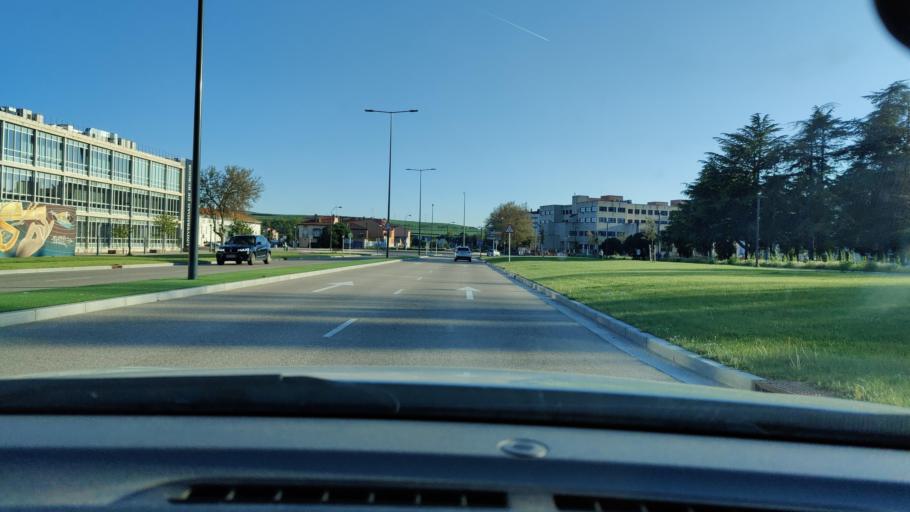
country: ES
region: Castille and Leon
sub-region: Provincia de Burgos
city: Villagonzalo-Pedernales
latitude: 42.3434
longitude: -3.7282
